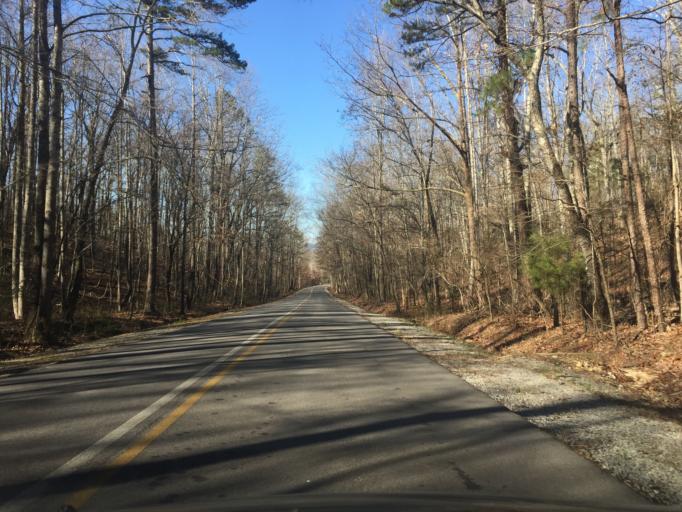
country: US
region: Tennessee
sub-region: Hamilton County
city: Harrison
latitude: 35.0865
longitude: -85.1215
